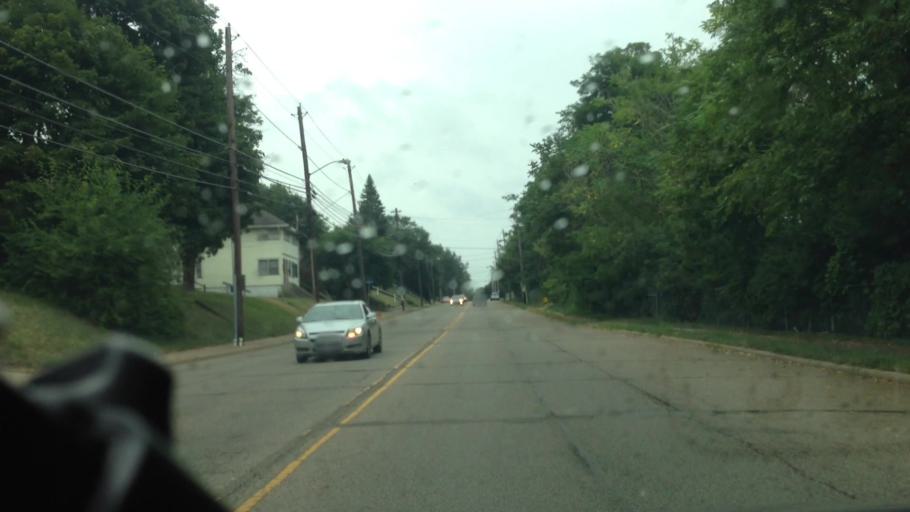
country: US
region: Ohio
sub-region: Stark County
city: Massillon
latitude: 40.7809
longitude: -81.5160
